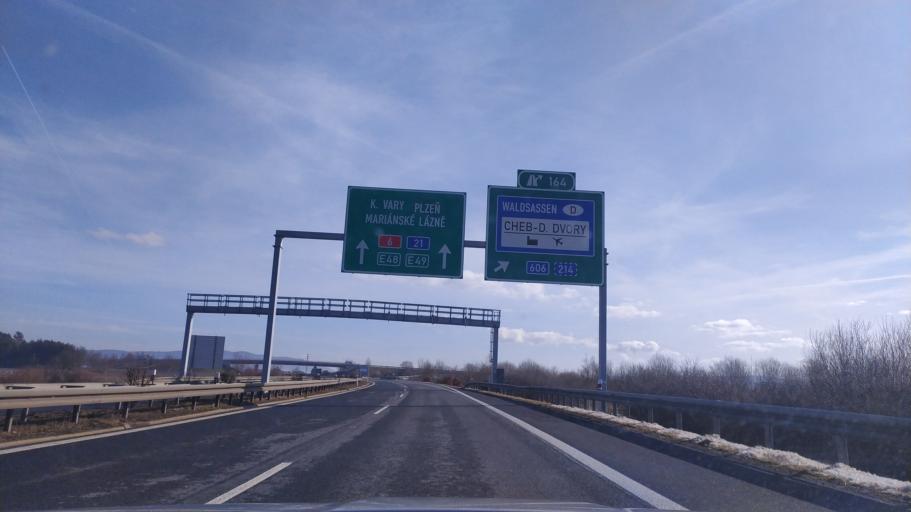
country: CZ
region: Karlovarsky
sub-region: Okres Cheb
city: Cheb
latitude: 50.0896
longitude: 12.4178
